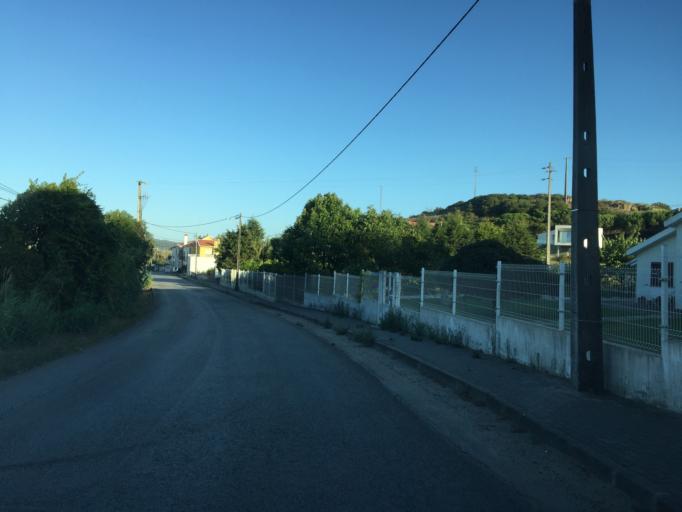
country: PT
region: Lisbon
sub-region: Torres Vedras
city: Torres Vedras
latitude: 39.0883
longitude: -9.2725
